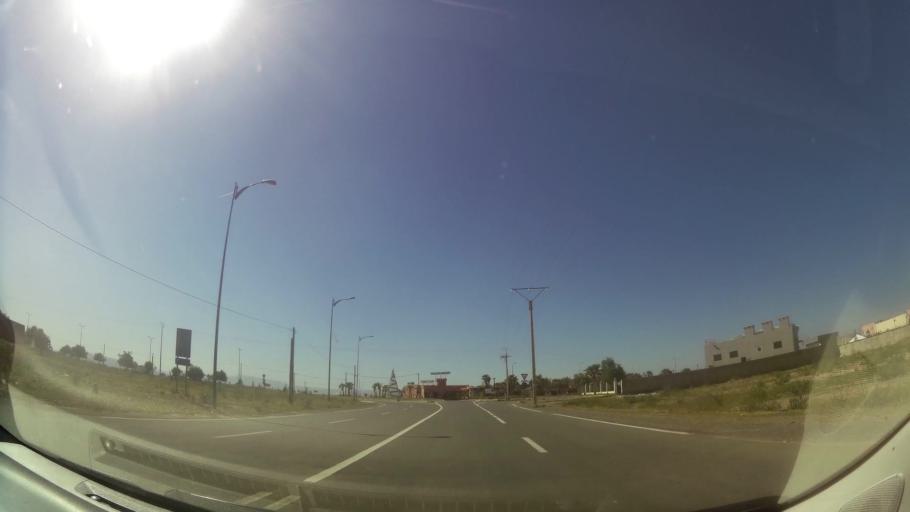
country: MA
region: Oriental
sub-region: Oujda-Angad
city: Oujda
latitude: 34.7313
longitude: -1.8724
